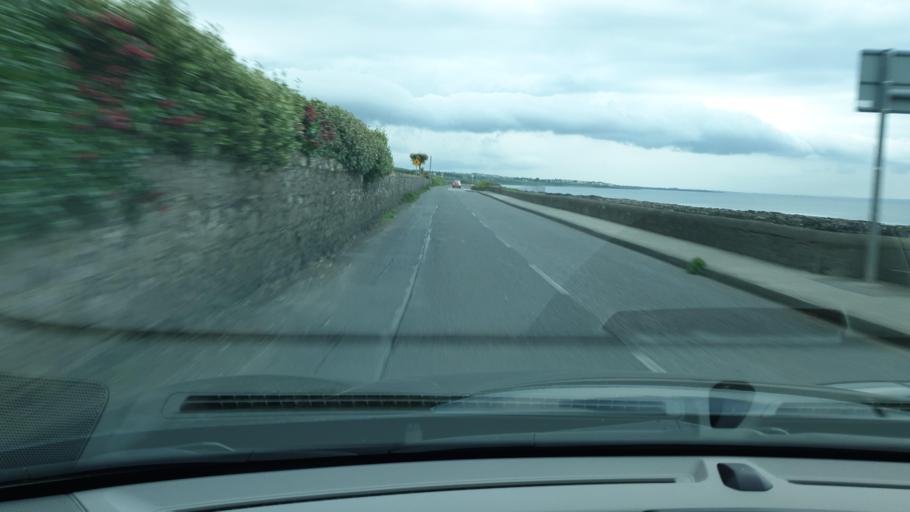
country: IE
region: Leinster
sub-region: Fingal County
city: Skerries
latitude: 53.5844
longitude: -6.1264
